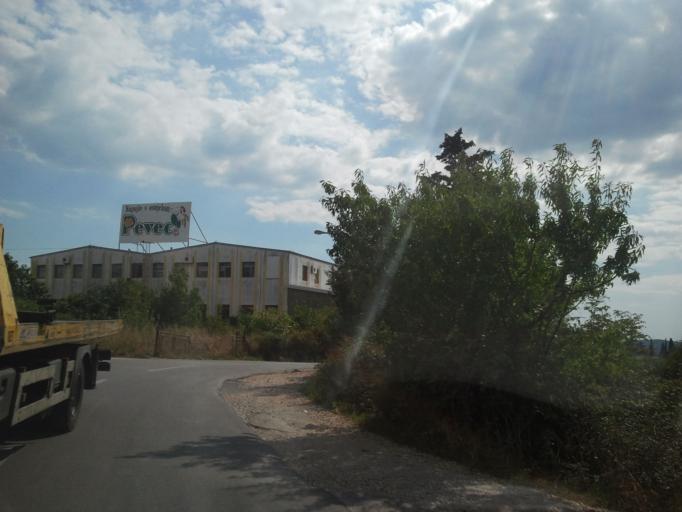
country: HR
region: Zadarska
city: Zadar
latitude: 44.1076
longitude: 15.2609
